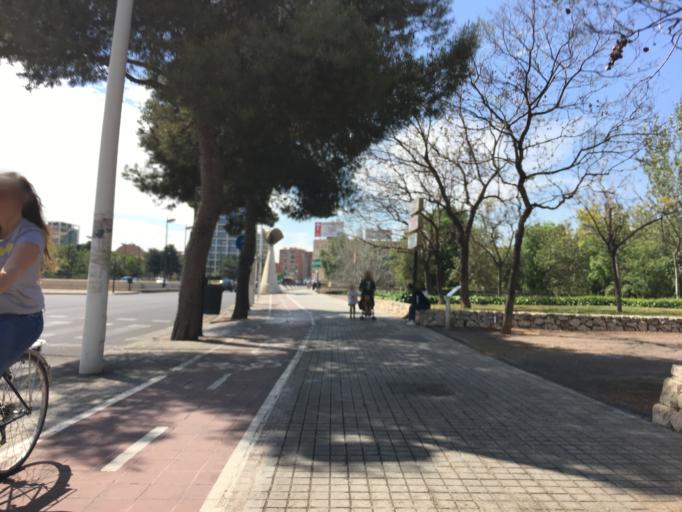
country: ES
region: Valencia
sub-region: Provincia de Valencia
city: Mislata
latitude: 39.4750
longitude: -0.4063
